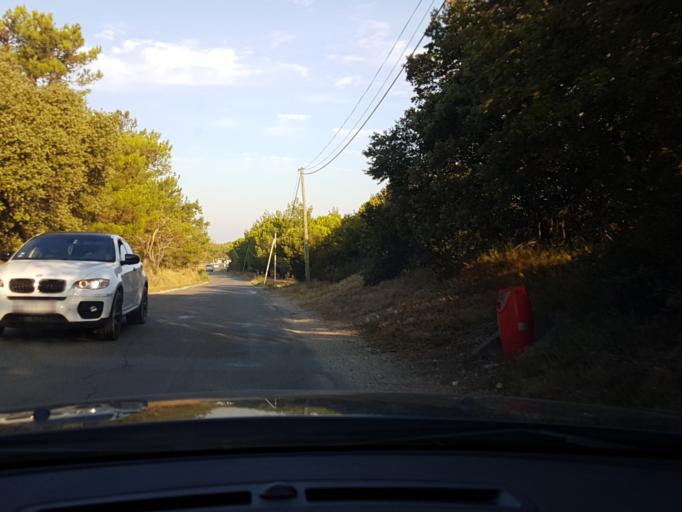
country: FR
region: Provence-Alpes-Cote d'Azur
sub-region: Departement des Bouches-du-Rhone
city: Eygalieres
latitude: 43.7642
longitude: 4.9304
